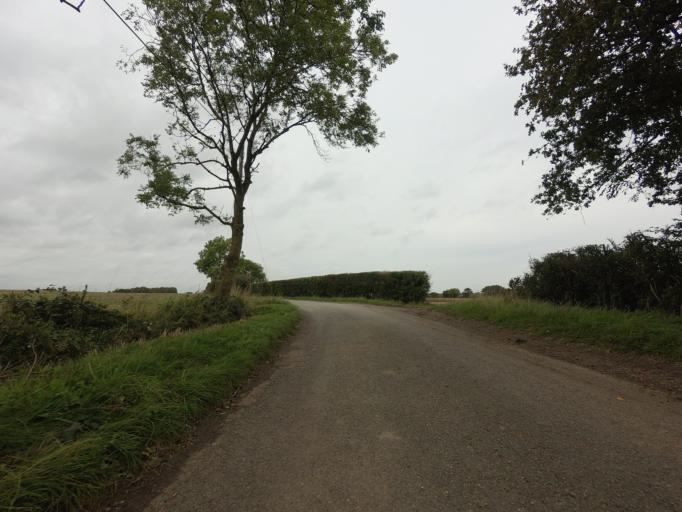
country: GB
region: England
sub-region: Hertfordshire
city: Reed
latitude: 51.9798
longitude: 0.0912
